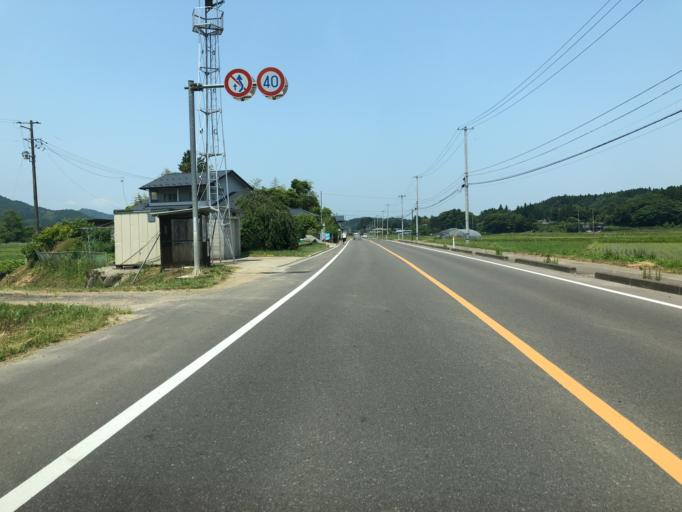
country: JP
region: Miyagi
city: Marumori
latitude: 37.8781
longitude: 140.8225
